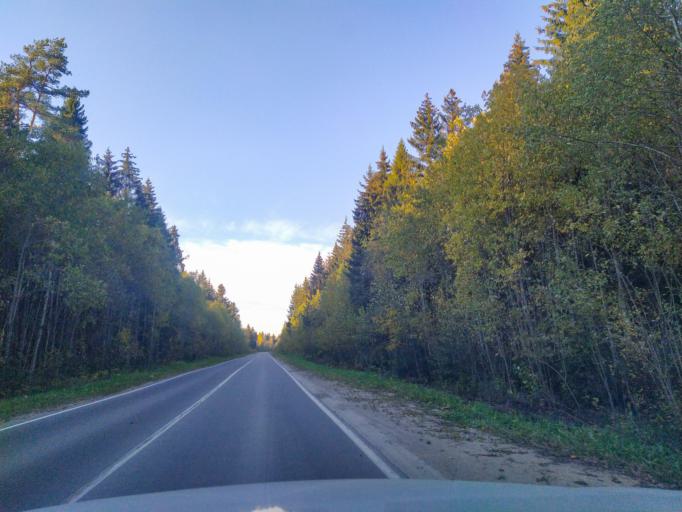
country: RU
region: Leningrad
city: Siverskiy
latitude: 59.3044
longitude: 30.0338
